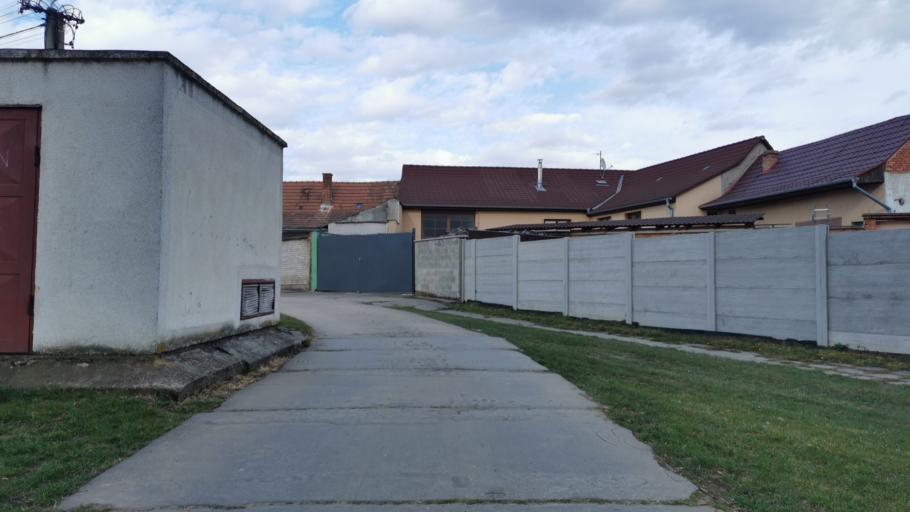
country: SK
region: Trnavsky
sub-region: Okres Skalica
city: Holic
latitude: 48.8042
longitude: 17.1953
